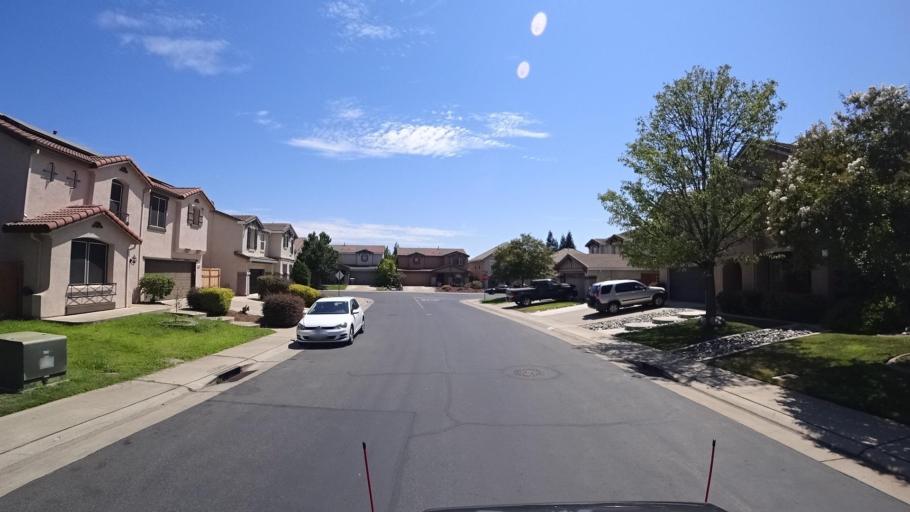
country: US
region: California
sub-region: Placer County
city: Rocklin
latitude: 38.8028
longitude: -121.2788
